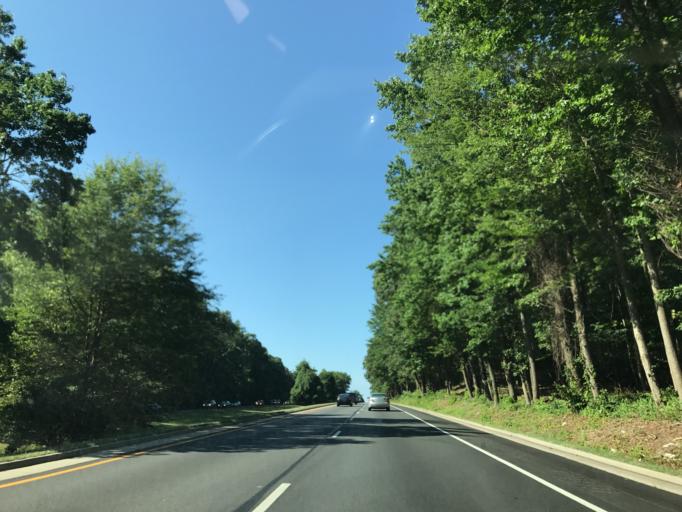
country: US
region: Maryland
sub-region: Prince George's County
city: Greenbelt
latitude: 39.0176
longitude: -76.8594
